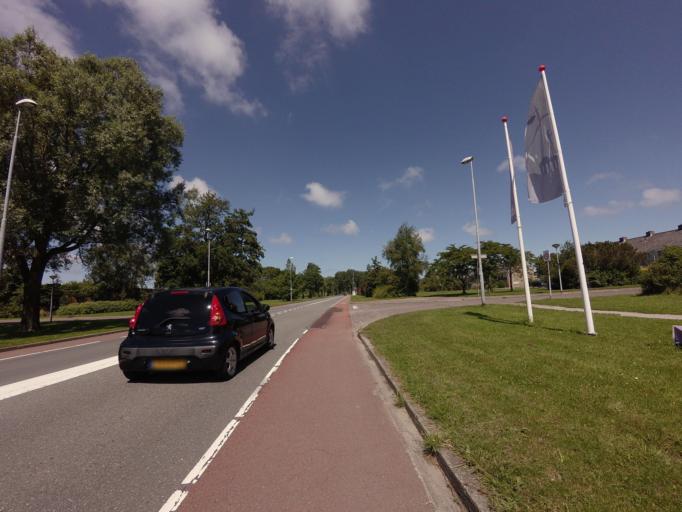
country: NL
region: North Holland
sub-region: Gemeente Den Helder
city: Den Helder
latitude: 52.9311
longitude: 4.7790
